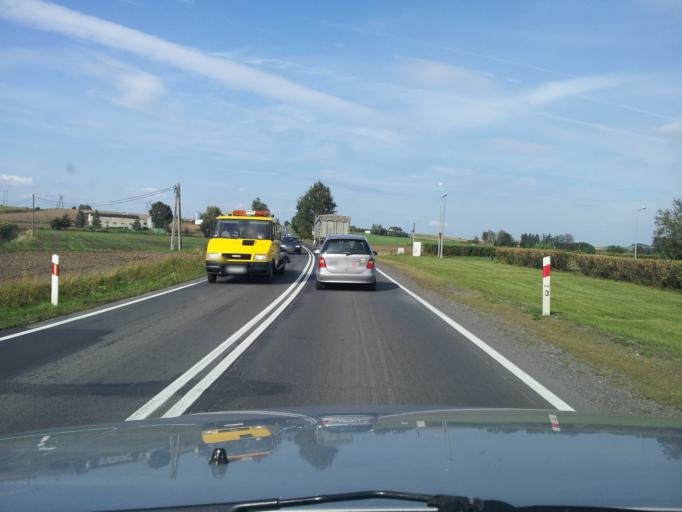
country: PL
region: Warmian-Masurian Voivodeship
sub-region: Powiat ilawski
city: Lubawa
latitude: 53.5129
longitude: 19.7451
